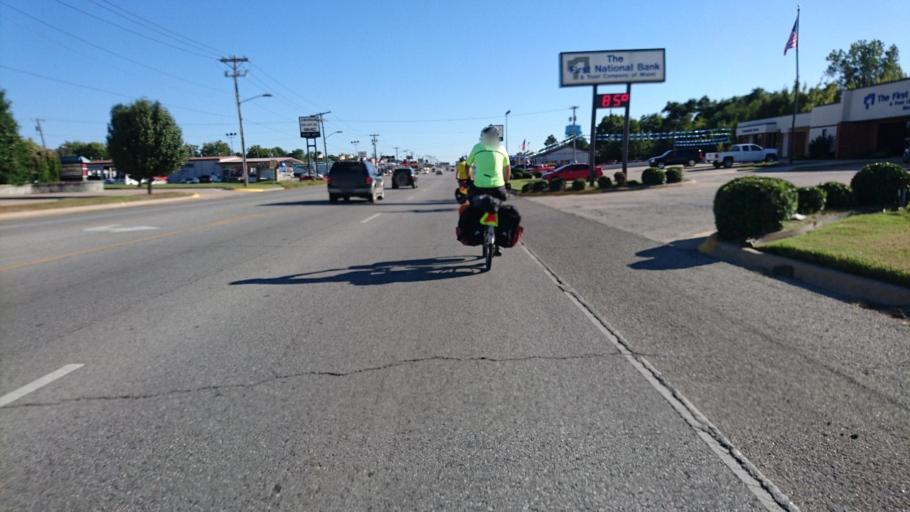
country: US
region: Oklahoma
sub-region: Ottawa County
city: Miami
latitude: 36.8953
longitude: -94.8776
